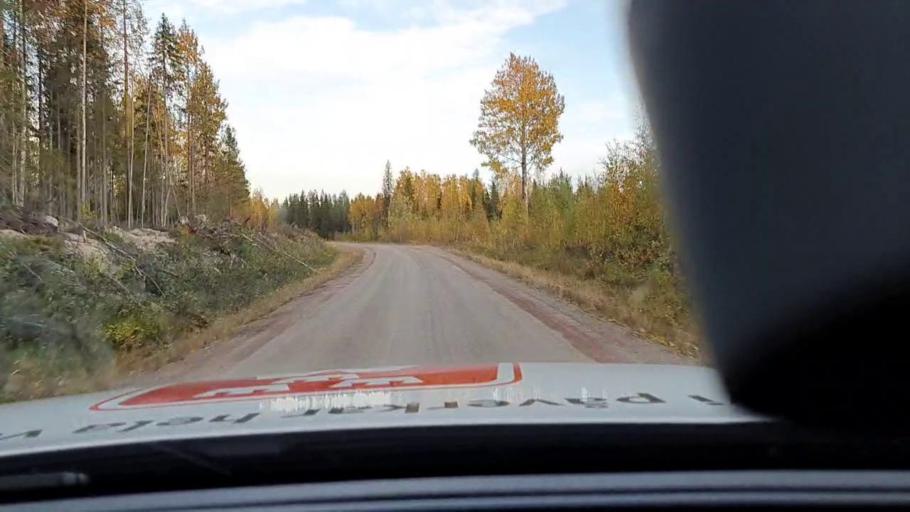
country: SE
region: Norrbotten
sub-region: Overkalix Kommun
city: OEverkalix
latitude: 66.3180
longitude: 22.6667
